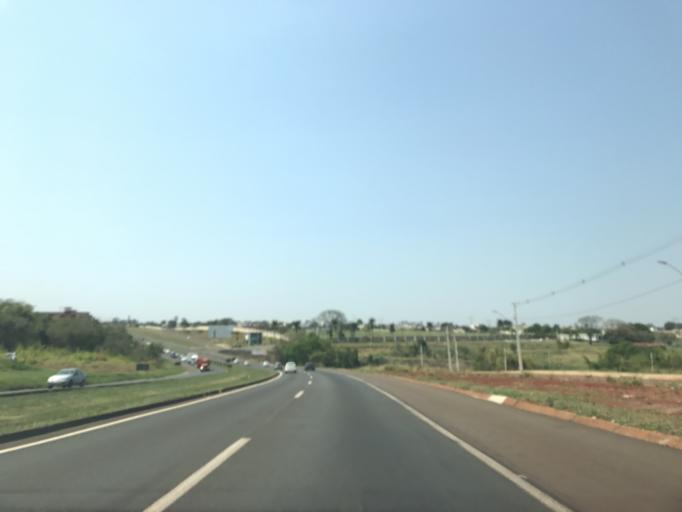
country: BR
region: Parana
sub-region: Cambe
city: Cambe
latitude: -23.2966
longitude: -51.2739
